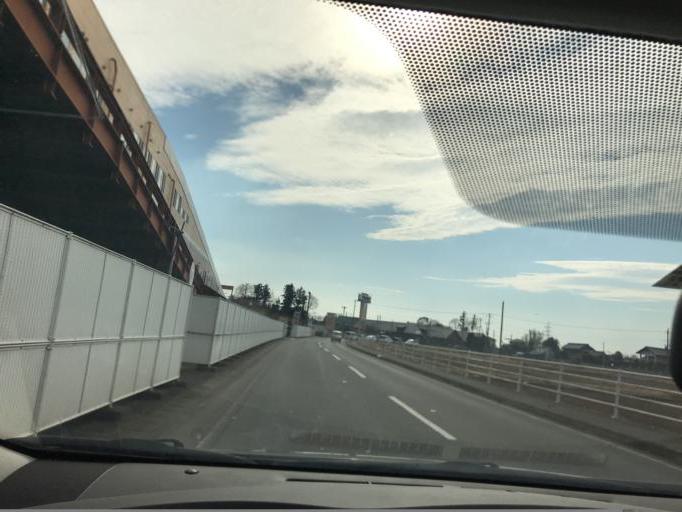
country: JP
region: Ibaraki
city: Naka
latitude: 36.0768
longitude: 140.0701
